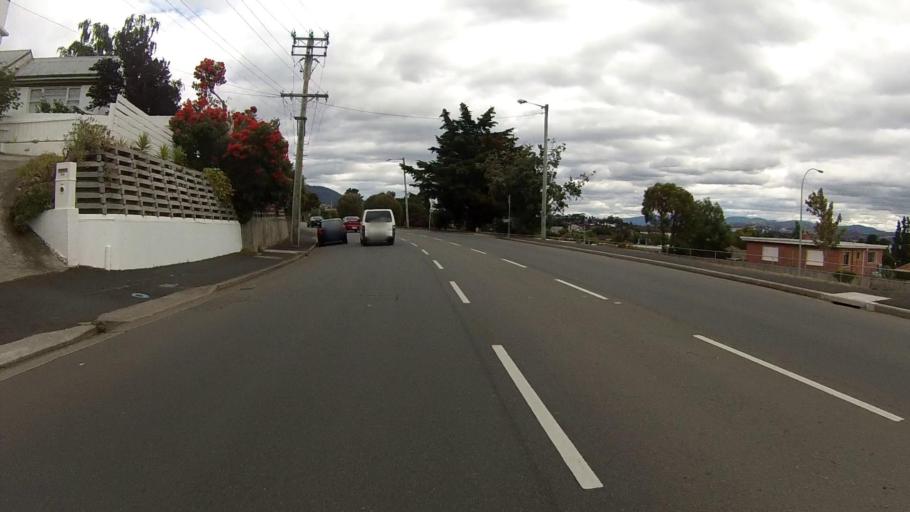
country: AU
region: Tasmania
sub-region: Glenorchy
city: Berriedale
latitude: -42.8219
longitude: 147.2634
